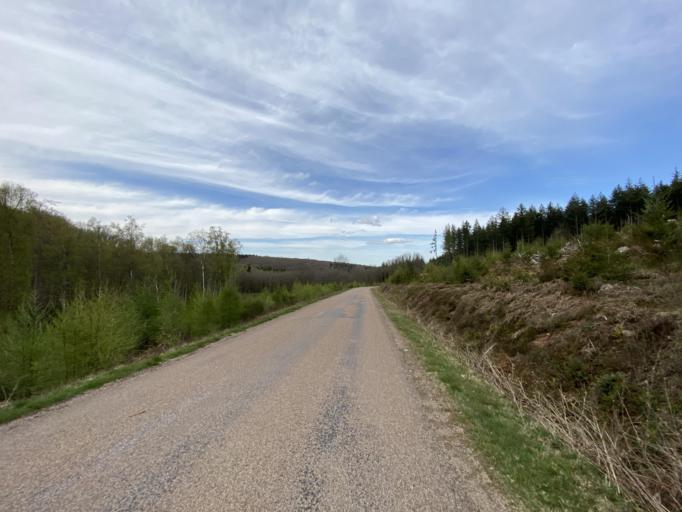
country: FR
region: Bourgogne
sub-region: Departement de la Cote-d'Or
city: Saulieu
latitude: 47.3076
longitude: 4.0876
